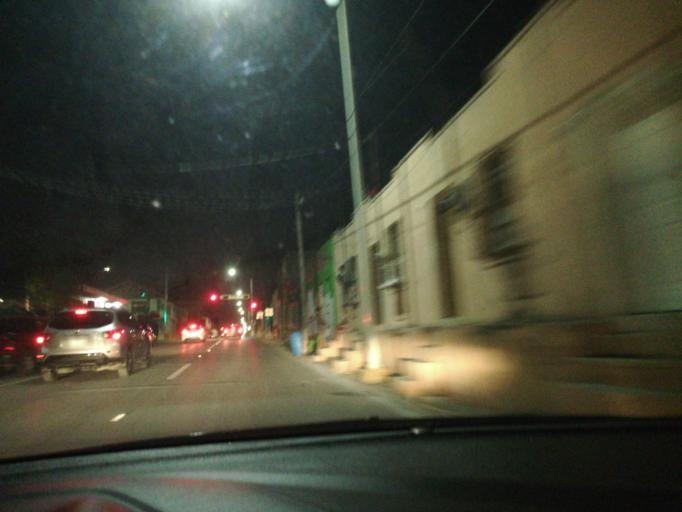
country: US
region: Texas
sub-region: Webb County
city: Laredo
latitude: 27.4935
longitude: -99.5017
